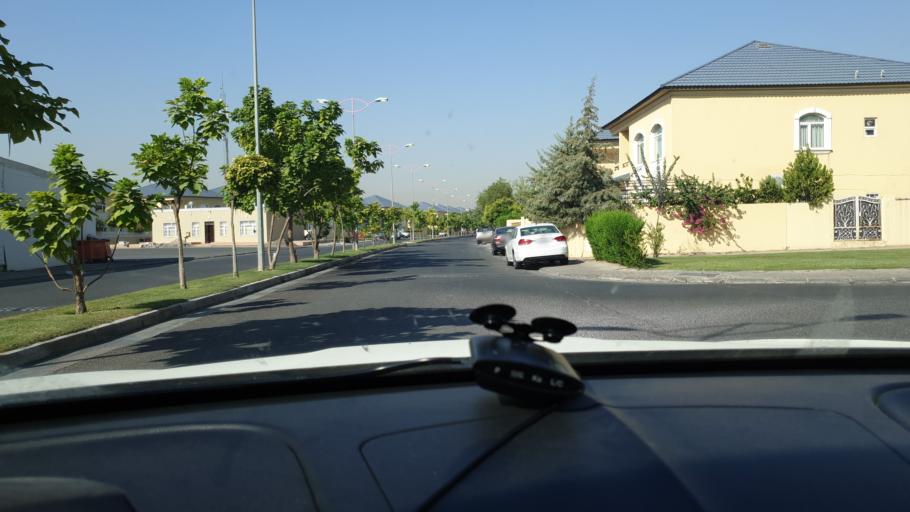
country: IQ
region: Arbil
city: Erbil
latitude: 36.1887
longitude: 43.9695
